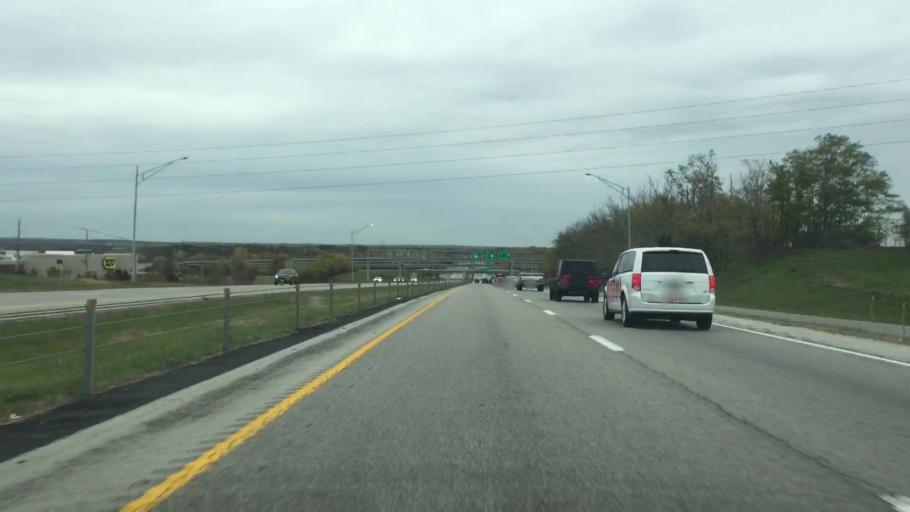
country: US
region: Missouri
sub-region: Jackson County
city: Lees Summit
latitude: 38.9279
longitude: -94.4045
